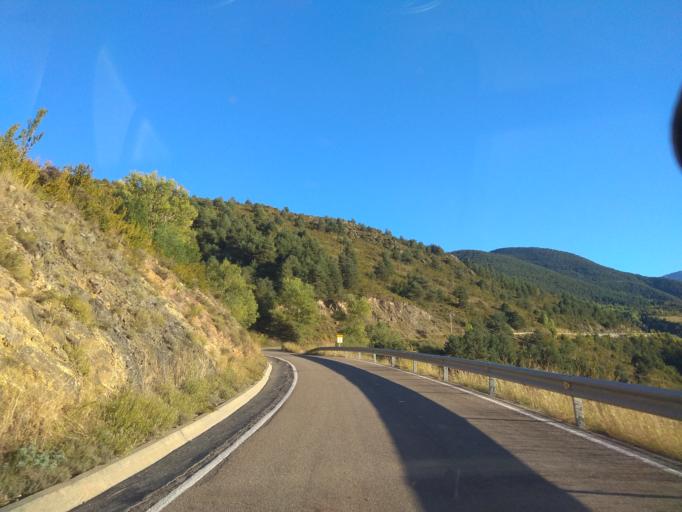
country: ES
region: Catalonia
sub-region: Provincia de Lleida
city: Lles de Cerdanya
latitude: 42.3551
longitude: 1.6890
